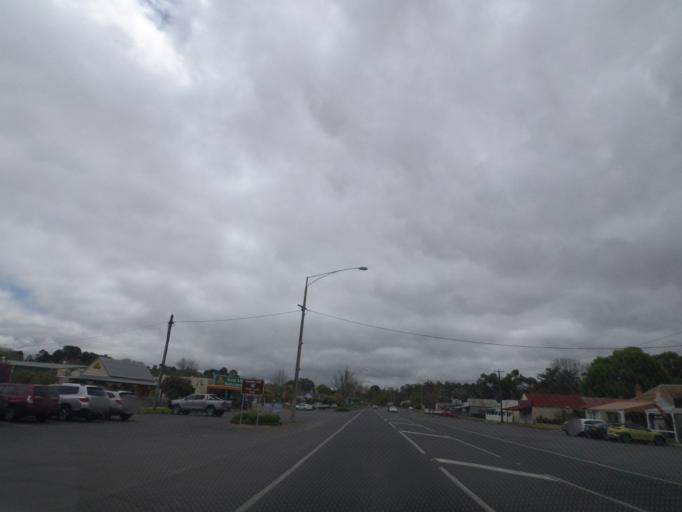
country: AU
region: Victoria
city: Brown Hill
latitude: -37.4213
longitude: 143.8947
